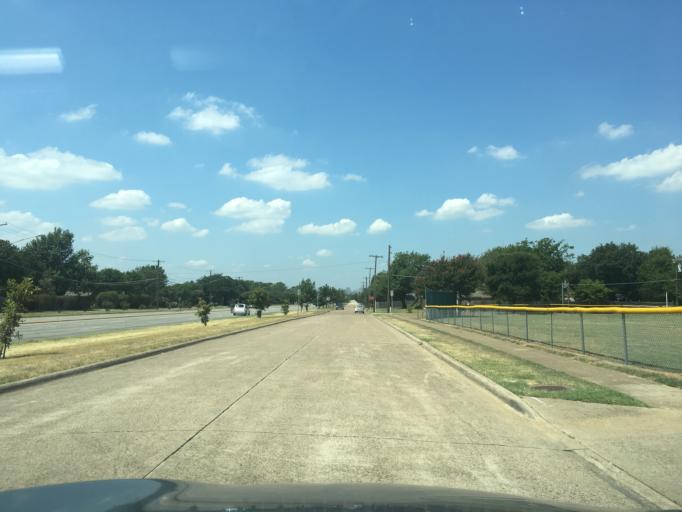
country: US
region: Texas
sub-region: Dallas County
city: Garland
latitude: 32.8644
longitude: -96.6874
